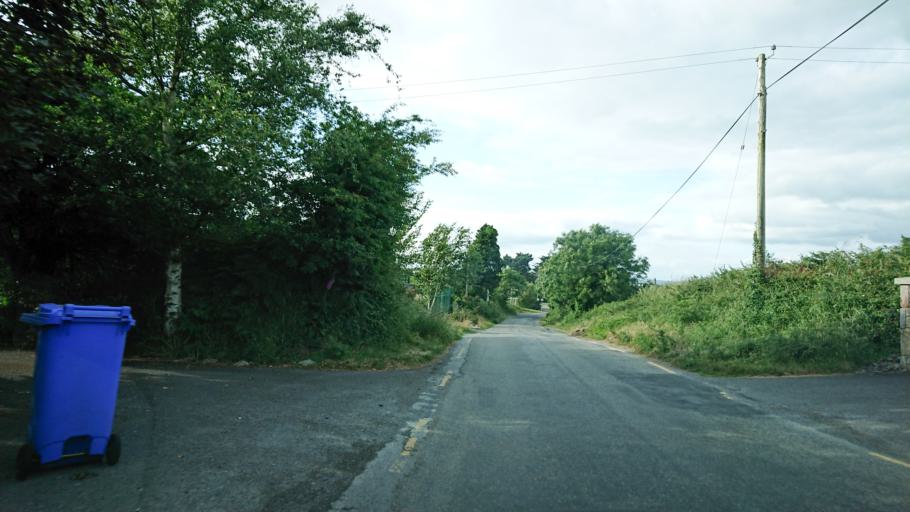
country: IE
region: Munster
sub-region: Waterford
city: Waterford
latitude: 52.2354
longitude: -7.1577
